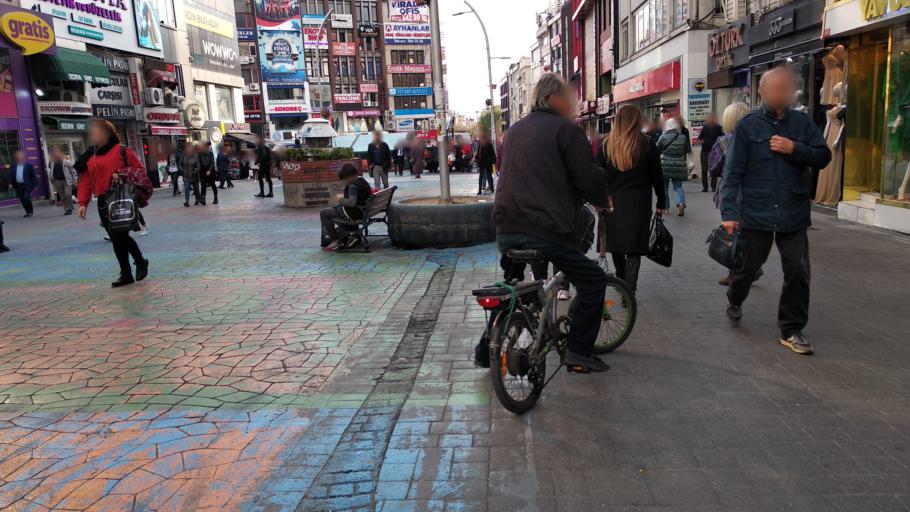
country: TR
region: Istanbul
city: Bahcelievler
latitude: 40.9791
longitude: 28.8743
